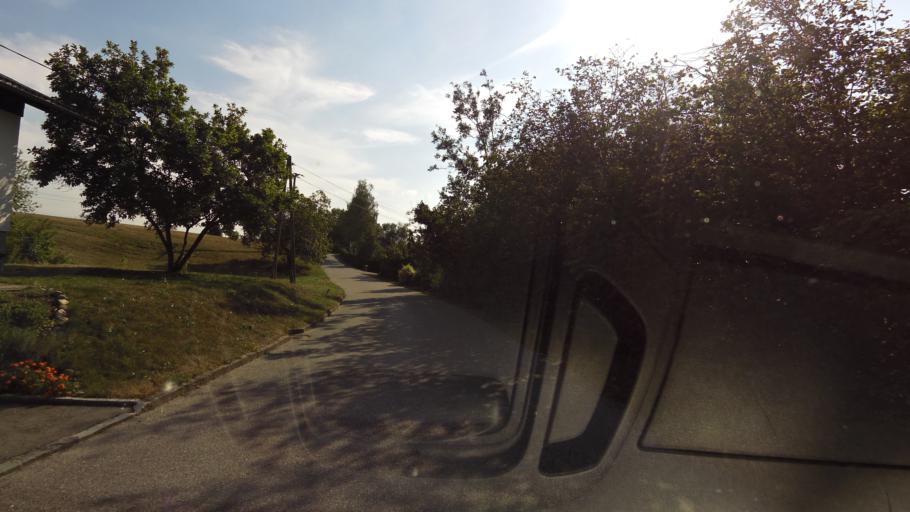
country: DE
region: Bavaria
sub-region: Lower Bavaria
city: Stubenberg
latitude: 48.2677
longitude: 13.0985
